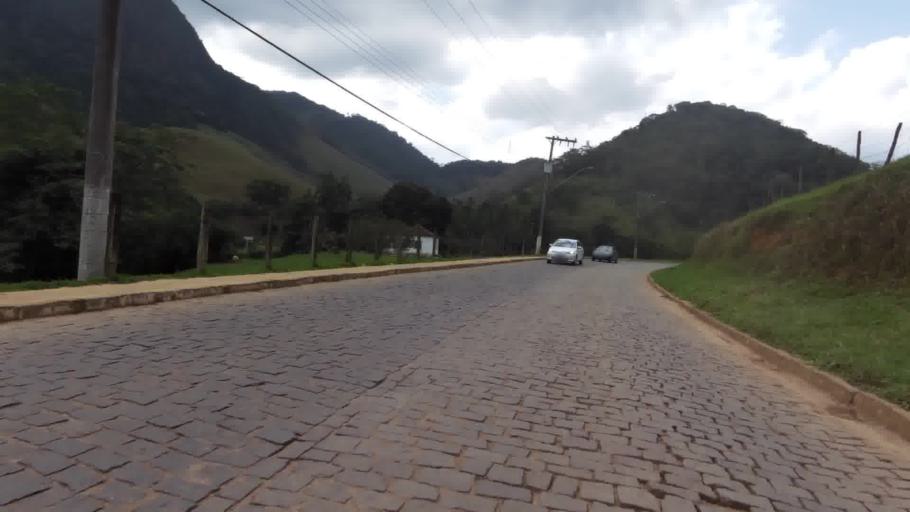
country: BR
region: Espirito Santo
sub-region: Alfredo Chaves
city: Alfredo Chaves
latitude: -20.6317
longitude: -40.7565
